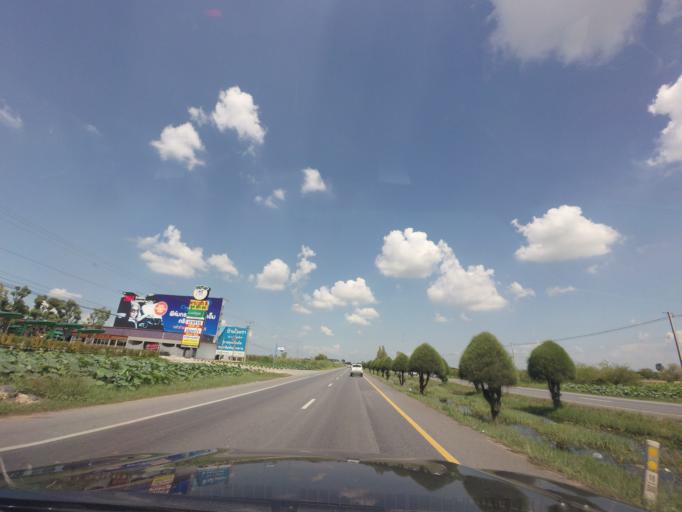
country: TH
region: Nakhon Ratchasima
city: Nakhon Ratchasima
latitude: 15.0544
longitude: 102.1417
